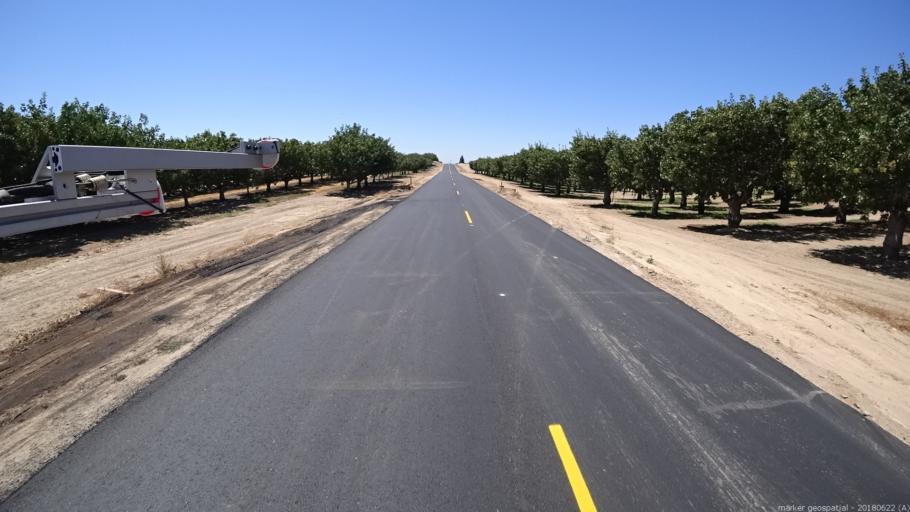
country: US
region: California
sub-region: Madera County
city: Bonadelle Ranchos-Madera Ranchos
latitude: 36.9090
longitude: -119.8577
